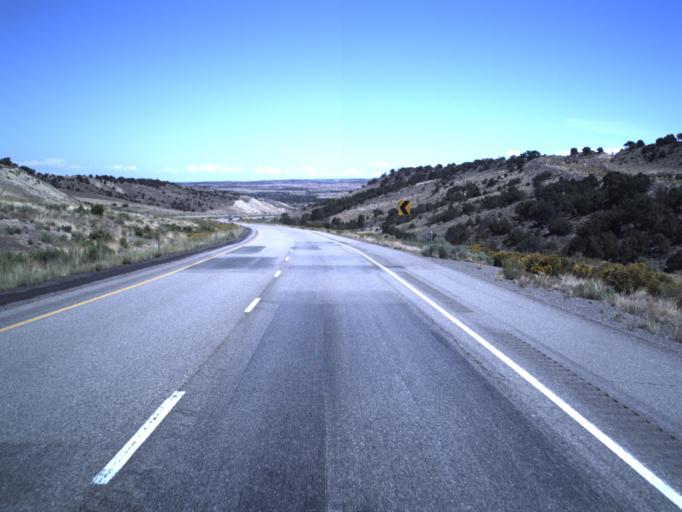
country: US
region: Utah
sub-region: Emery County
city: Ferron
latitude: 38.7837
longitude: -111.3040
